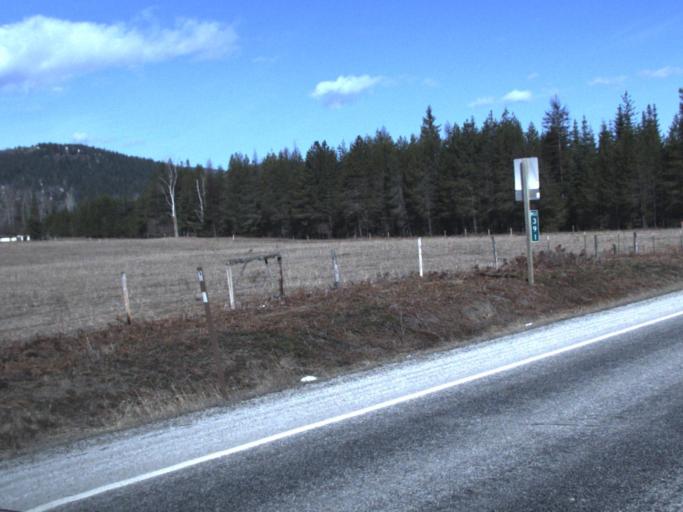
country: CA
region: British Columbia
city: Fruitvale
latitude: 48.6769
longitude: -117.4014
